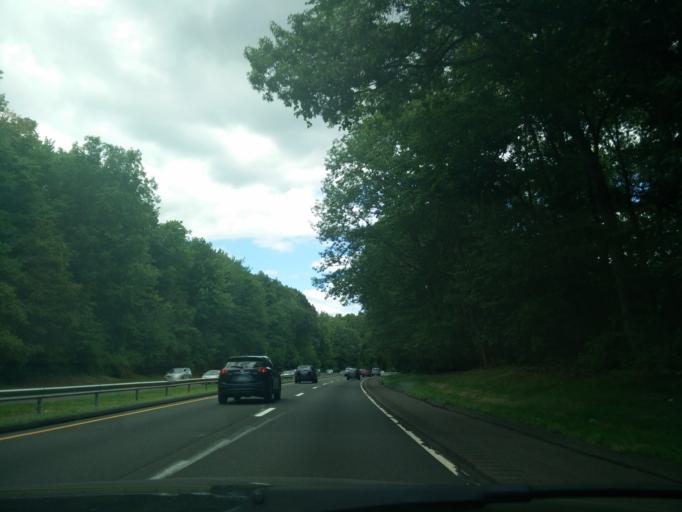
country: US
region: Connecticut
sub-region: New Haven County
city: Woodbridge
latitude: 41.3524
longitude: -72.9612
